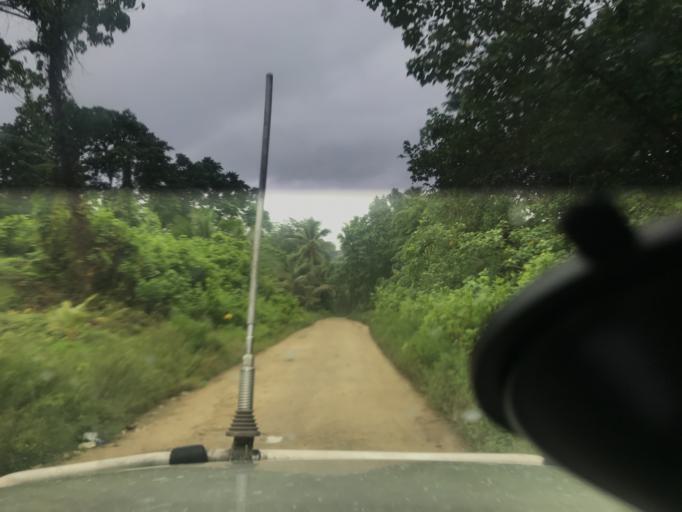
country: SB
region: Choiseul
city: Taro'a
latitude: -9.1739
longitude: 160.9178
